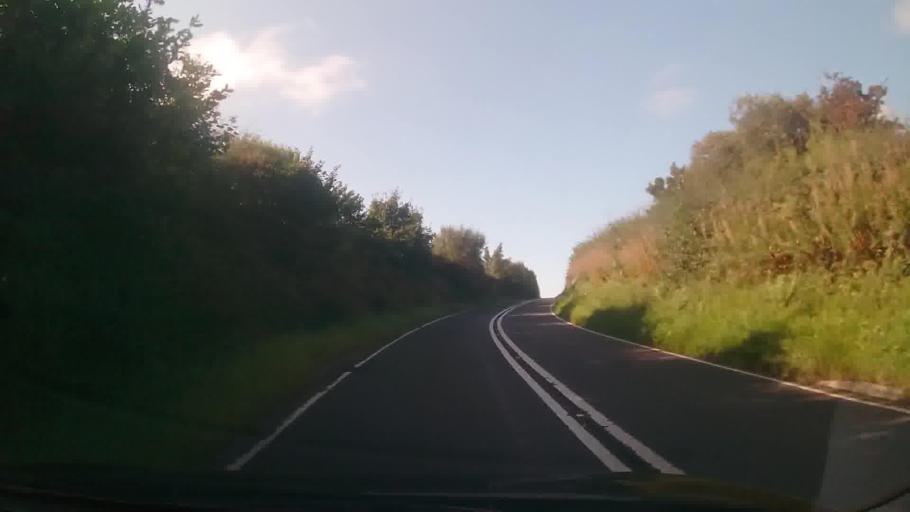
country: GB
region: England
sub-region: Cumbria
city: Seascale
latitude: 54.3378
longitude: -3.3633
